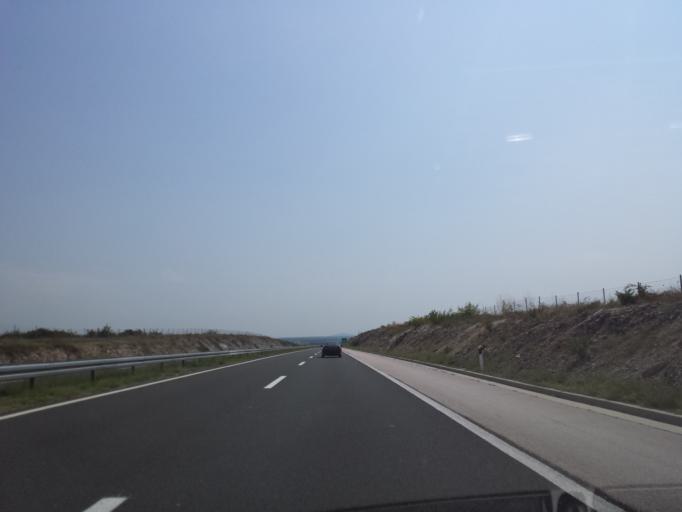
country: HR
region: Zadarska
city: Polaca
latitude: 44.0738
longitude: 15.5161
